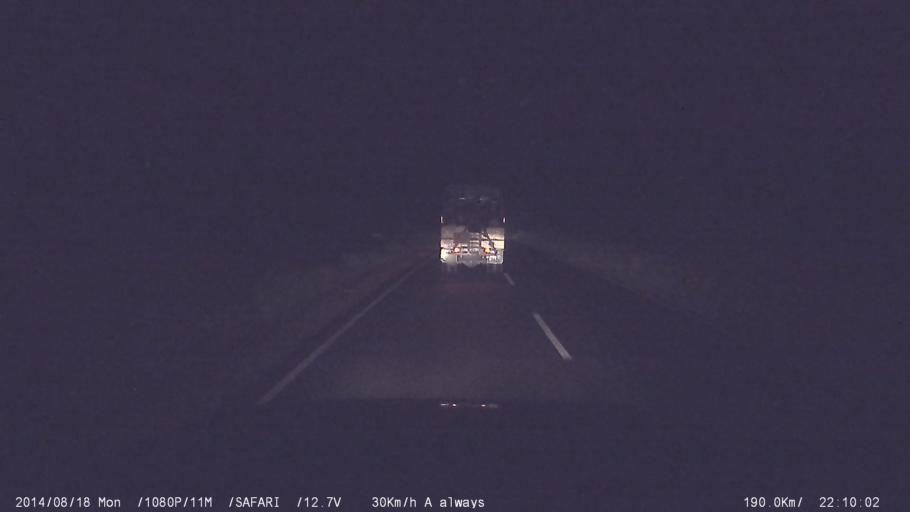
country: IN
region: Kerala
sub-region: Thrissur District
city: Chelakara
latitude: 10.5841
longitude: 76.4353
